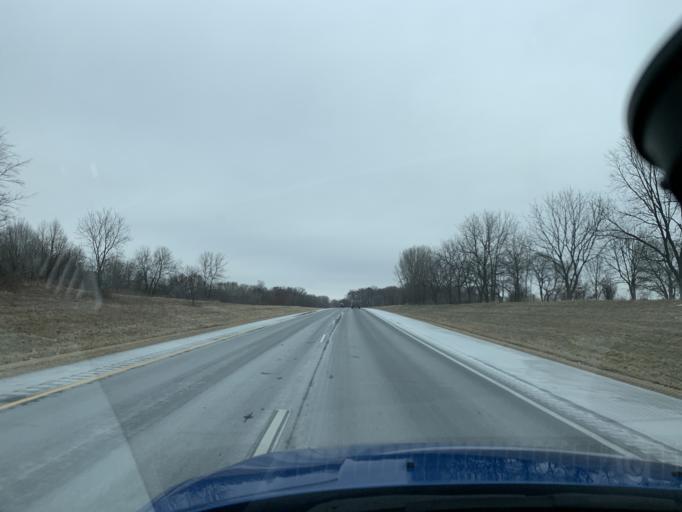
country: US
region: Wisconsin
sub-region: Dane County
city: Sun Prairie
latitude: 43.2275
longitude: -89.1583
